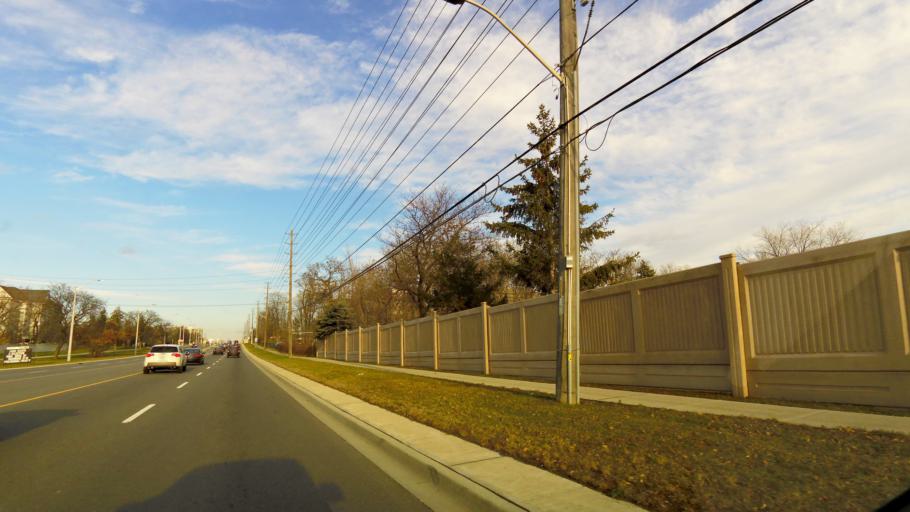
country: CA
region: Ontario
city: Etobicoke
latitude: 43.6191
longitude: -79.6062
